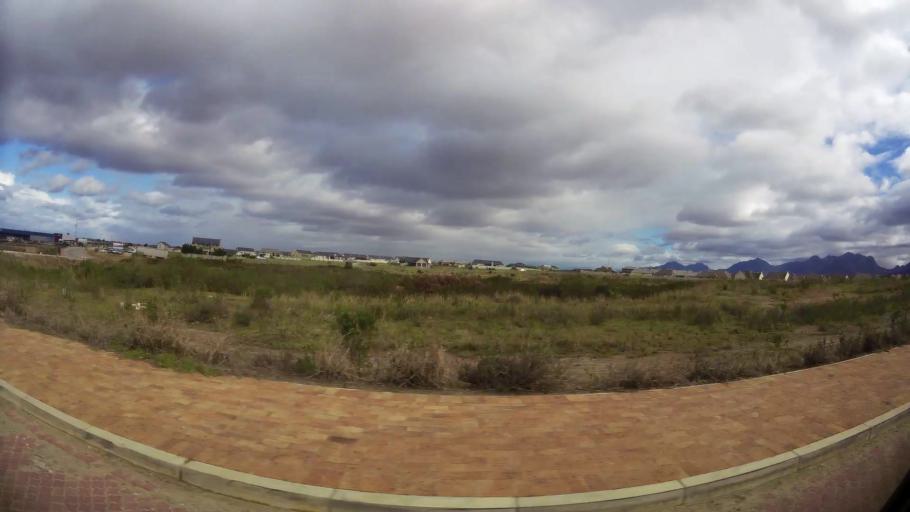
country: ZA
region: Western Cape
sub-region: Eden District Municipality
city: George
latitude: -33.9866
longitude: 22.4987
